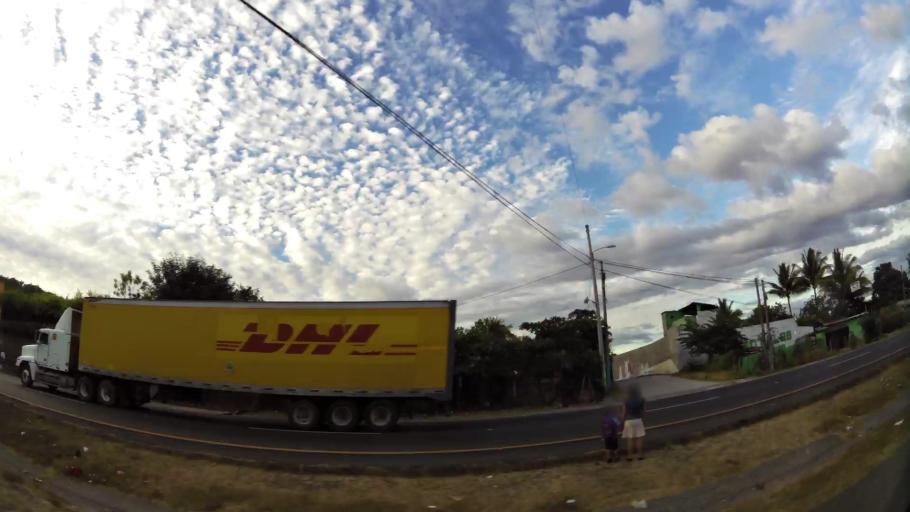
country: SV
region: Cuscatlan
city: Cojutepeque
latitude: 13.7298
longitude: -88.8962
